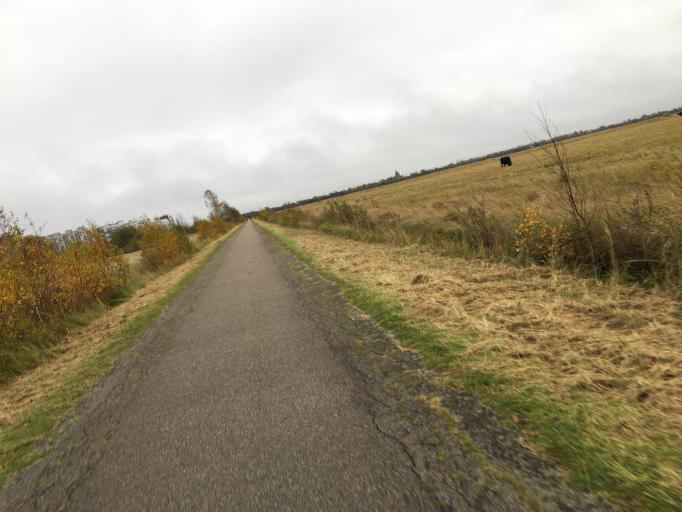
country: DK
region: Capital Region
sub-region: Tarnby Kommune
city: Tarnby
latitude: 55.6155
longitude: 12.5567
